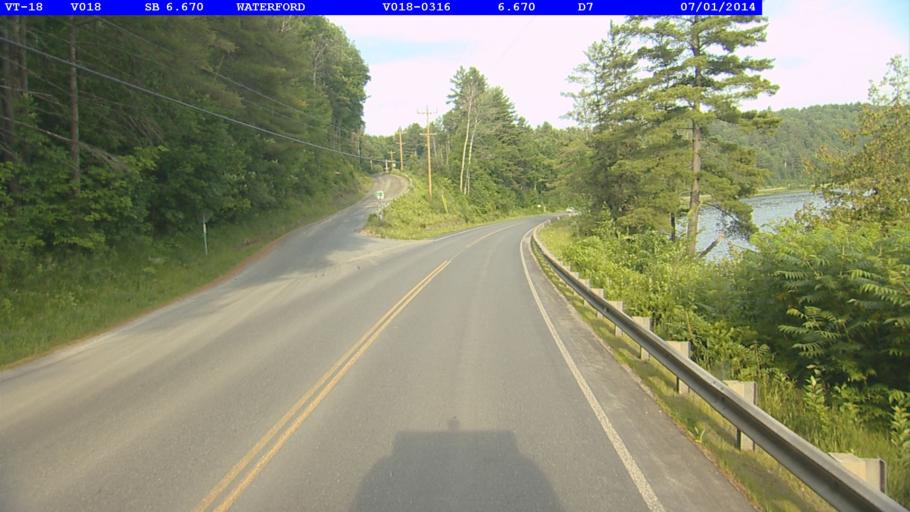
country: US
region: Vermont
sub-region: Caledonia County
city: Saint Johnsbury
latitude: 44.4225
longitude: -71.9418
